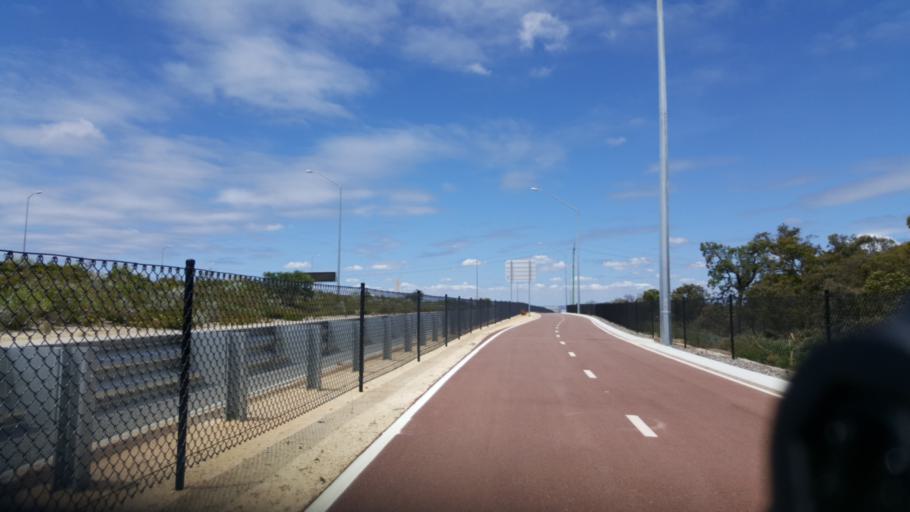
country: AU
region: Western Australia
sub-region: Bayswater
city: Embleton
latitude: -31.8679
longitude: 115.8990
